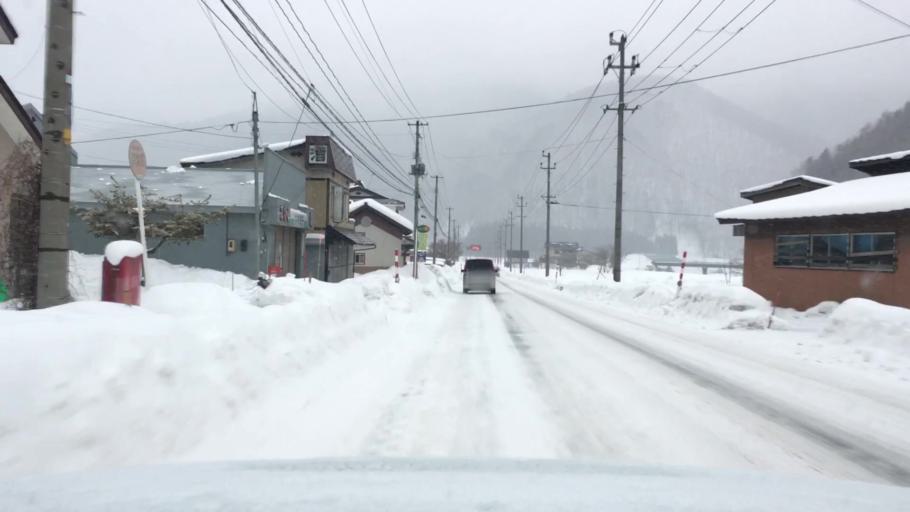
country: JP
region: Akita
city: Hanawa
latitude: 40.0762
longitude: 141.0212
